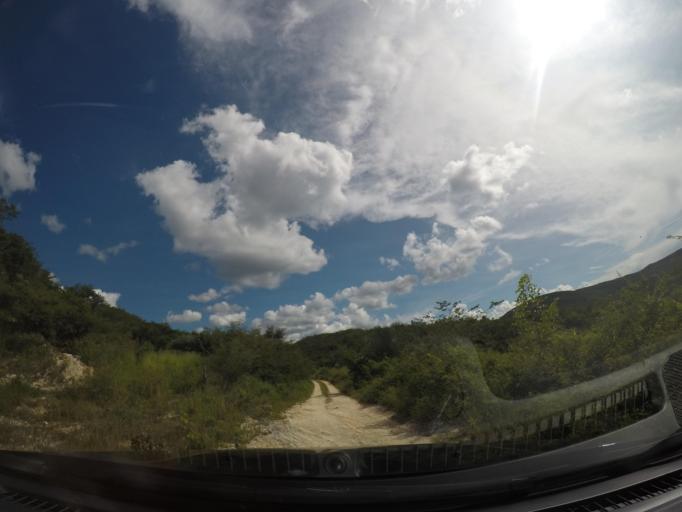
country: BR
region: Bahia
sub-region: Barra Da Estiva
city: Barra da Estiva
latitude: -13.1312
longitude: -41.5950
